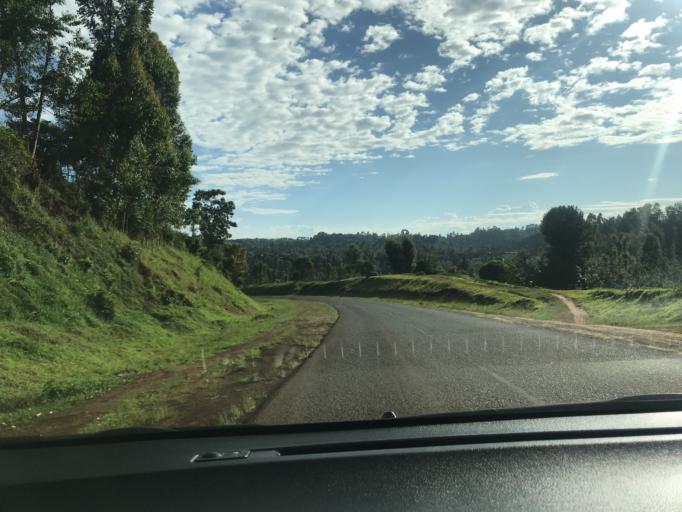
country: KE
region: Kirinyaga
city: Keruguya
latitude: -0.4837
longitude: 37.2145
